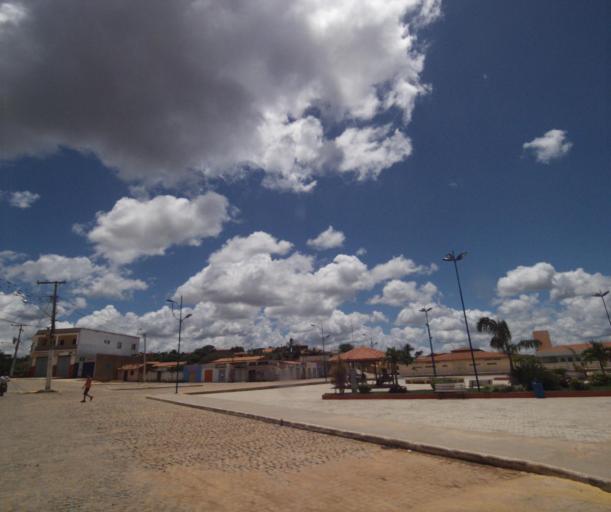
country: BR
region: Bahia
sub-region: Pocoes
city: Pocoes
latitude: -14.3759
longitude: -40.5060
